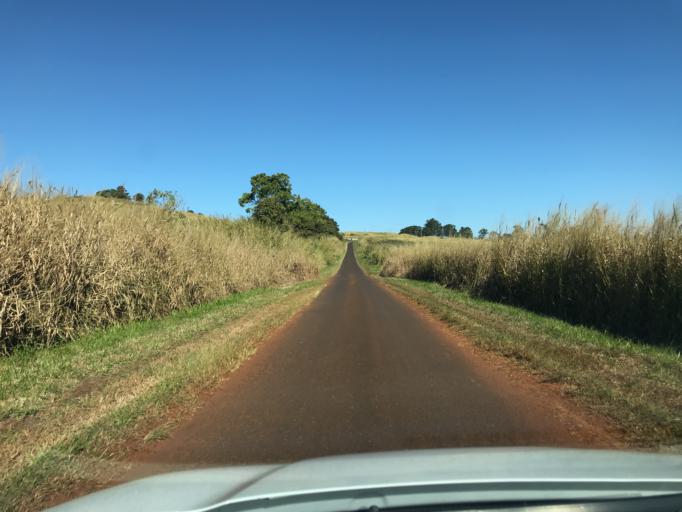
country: AU
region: Queensland
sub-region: Tablelands
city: Atherton
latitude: -17.2881
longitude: 145.5433
